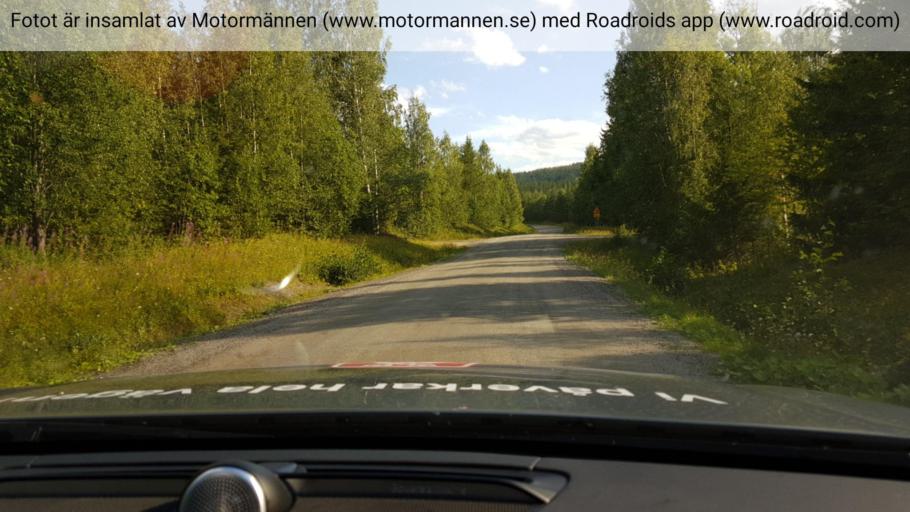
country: SE
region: Vaesternorrland
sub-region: Solleftea Kommun
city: As
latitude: 63.7720
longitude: 16.3168
